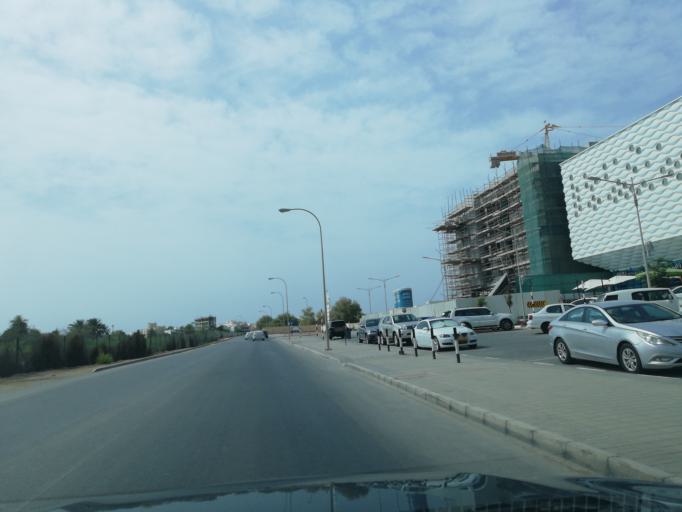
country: OM
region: Muhafazat Masqat
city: As Sib al Jadidah
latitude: 23.6223
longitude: 58.2491
